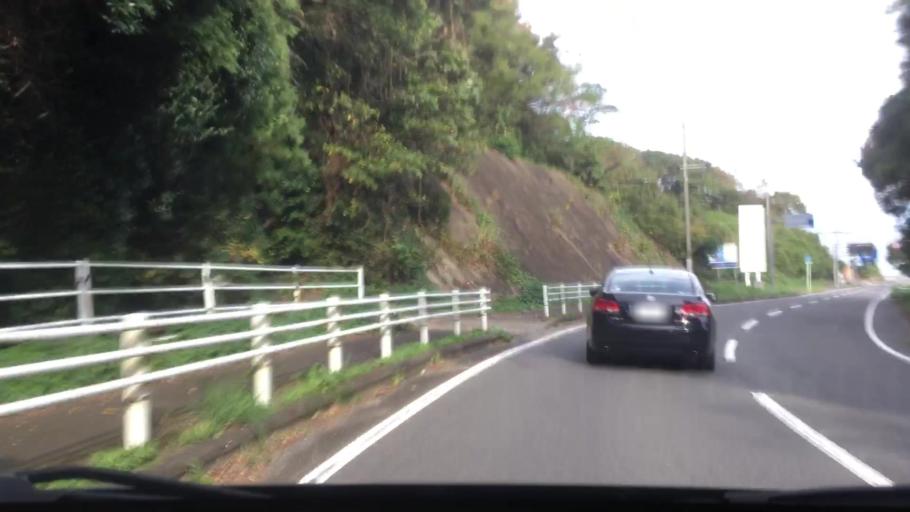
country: JP
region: Nagasaki
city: Sasebo
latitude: 33.0365
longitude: 129.6600
